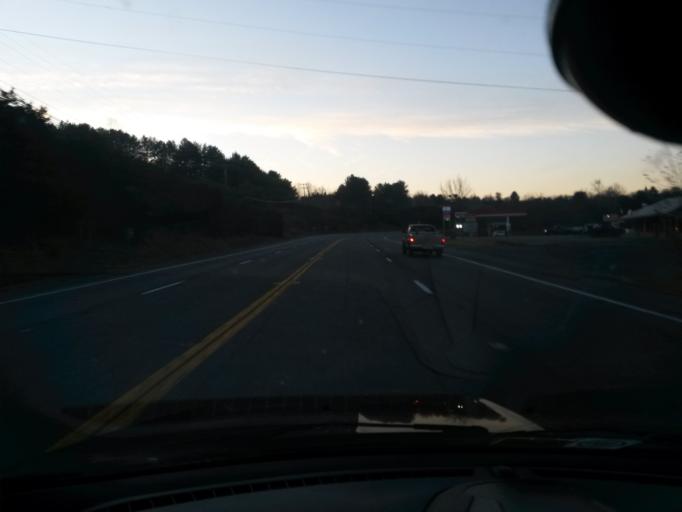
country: US
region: Virginia
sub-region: Botetourt County
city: Fincastle
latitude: 37.5082
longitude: -79.8777
